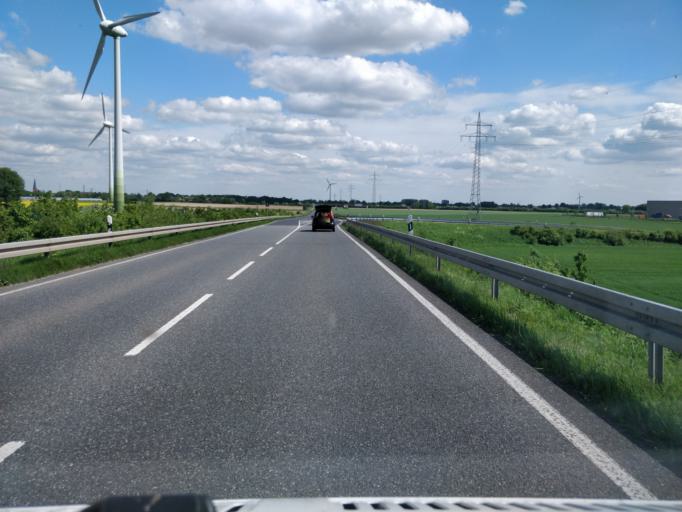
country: DE
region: North Rhine-Westphalia
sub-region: Regierungsbezirk Dusseldorf
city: Kleve
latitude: 51.8184
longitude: 6.1460
